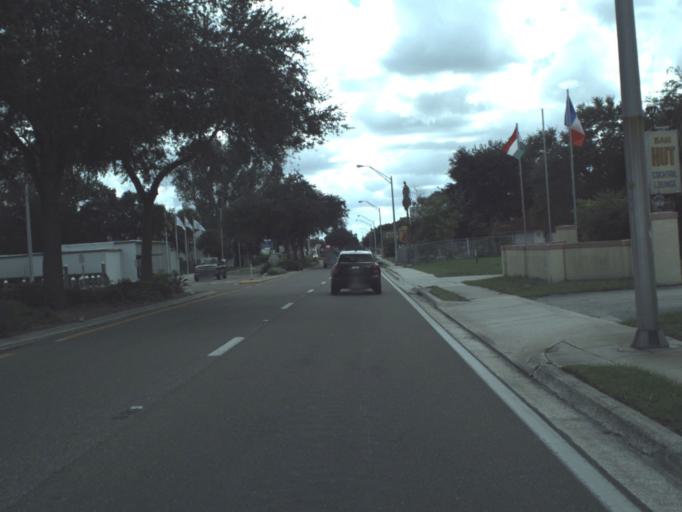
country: US
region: Florida
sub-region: Sarasota County
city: North Sarasota
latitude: 27.3734
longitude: -82.5539
